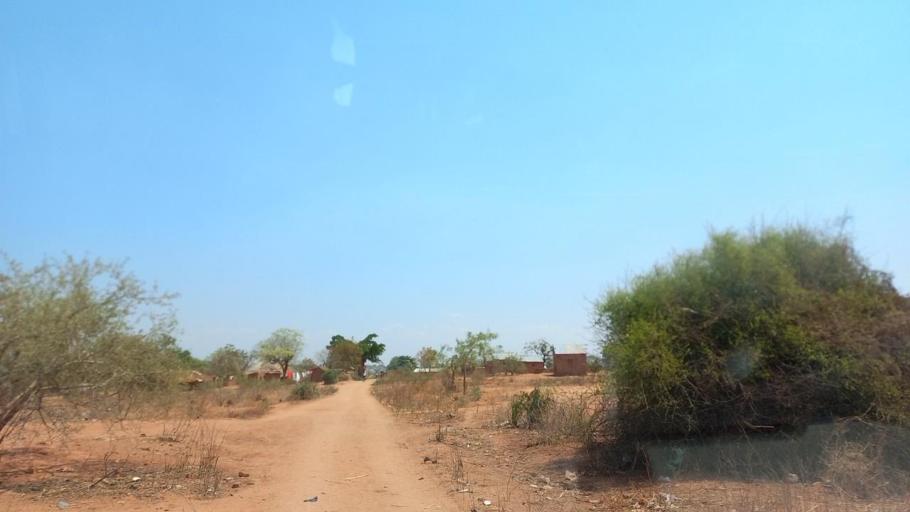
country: ZM
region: Lusaka
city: Luangwa
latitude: -15.6023
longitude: 30.4019
